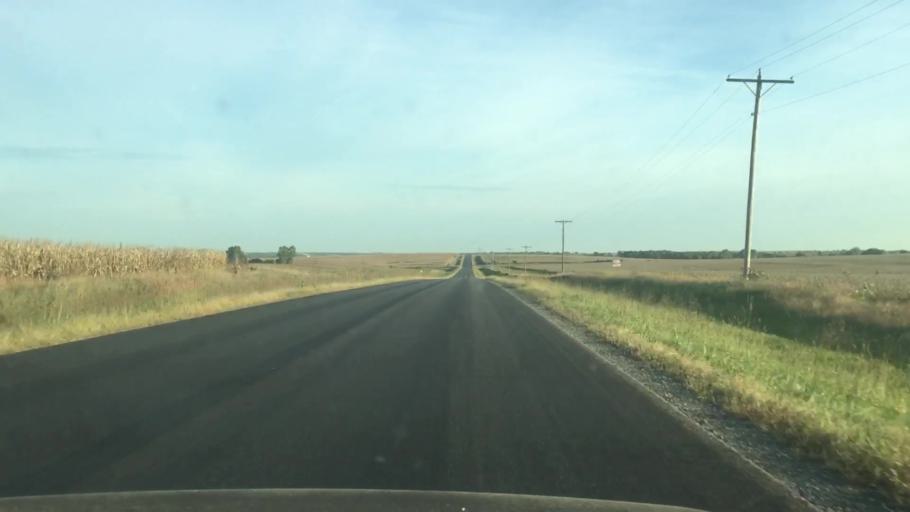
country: US
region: Kansas
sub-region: Marshall County
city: Marysville
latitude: 39.9078
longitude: -96.6010
